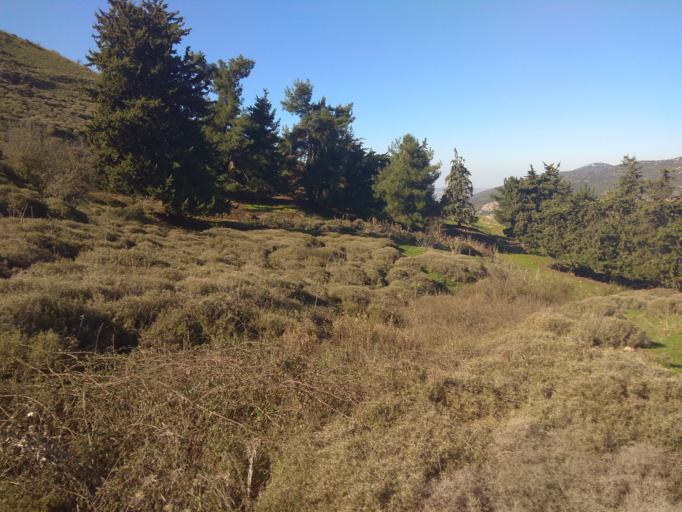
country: SY
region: Quneitra
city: Mas`adah
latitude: 33.2485
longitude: 35.7544
